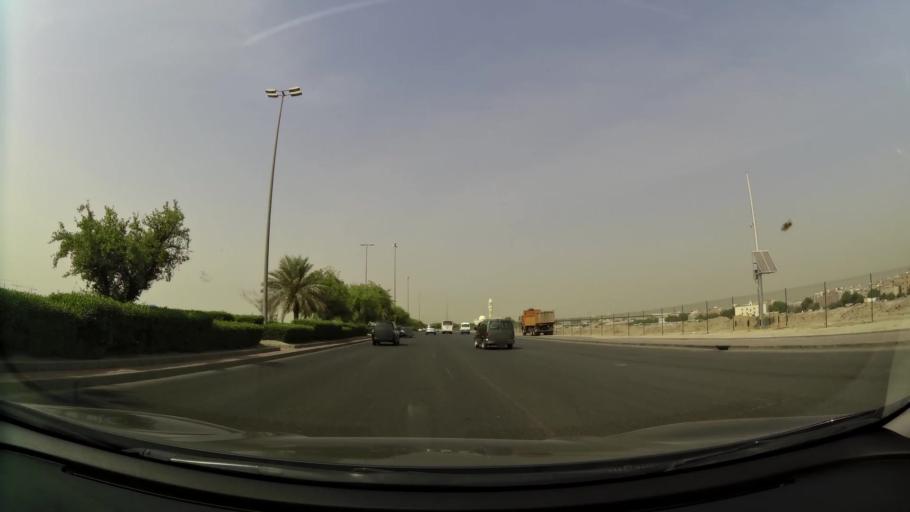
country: KW
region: Al Asimah
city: Ar Rabiyah
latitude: 29.2616
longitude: 47.9115
